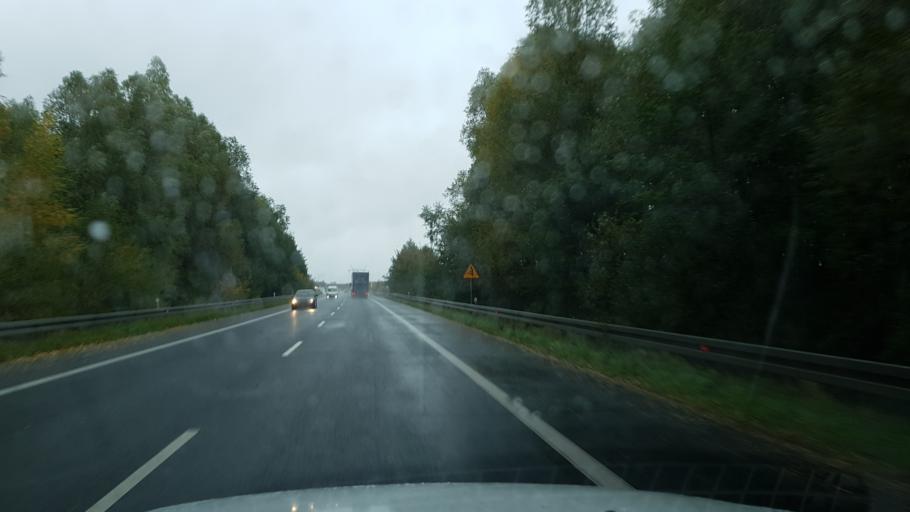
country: PL
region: West Pomeranian Voivodeship
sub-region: Powiat gryfinski
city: Stare Czarnowo
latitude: 53.2839
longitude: 14.7863
